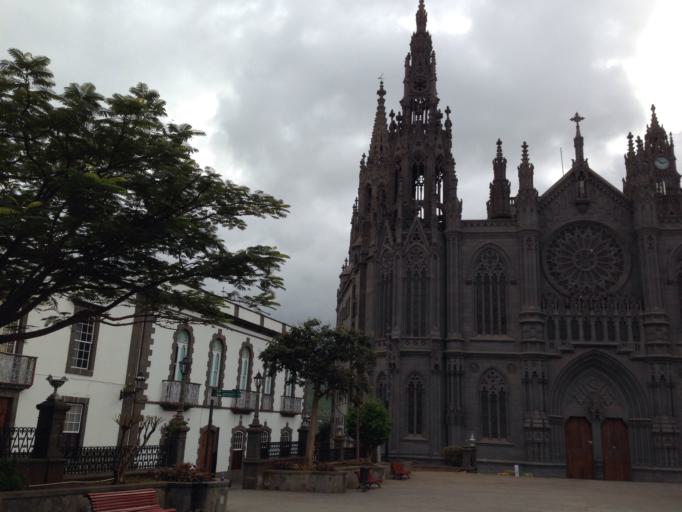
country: ES
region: Canary Islands
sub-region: Provincia de Las Palmas
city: Arucas
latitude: 28.1192
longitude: -15.5227
